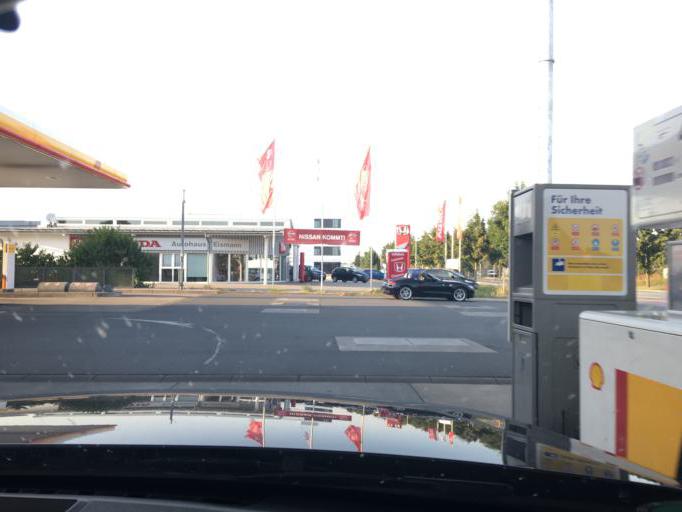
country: DE
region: Bavaria
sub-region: Upper Franconia
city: Forchheim
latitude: 49.7031
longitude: 11.0611
